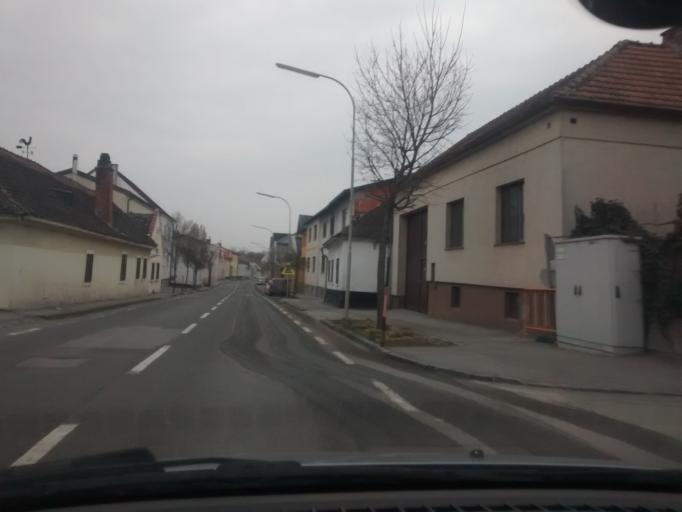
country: AT
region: Lower Austria
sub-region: Politischer Bezirk Wien-Umgebung
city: Moosbrunn
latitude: 48.0220
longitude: 16.4666
